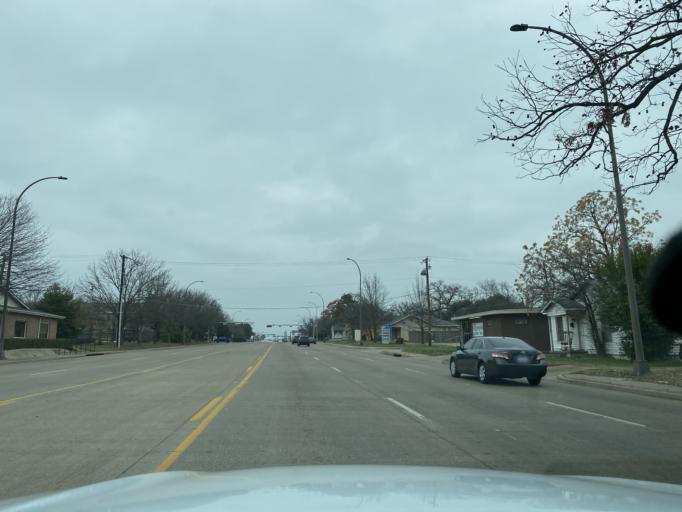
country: US
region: Texas
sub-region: Tarrant County
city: Arlington
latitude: 32.7320
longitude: -97.0974
